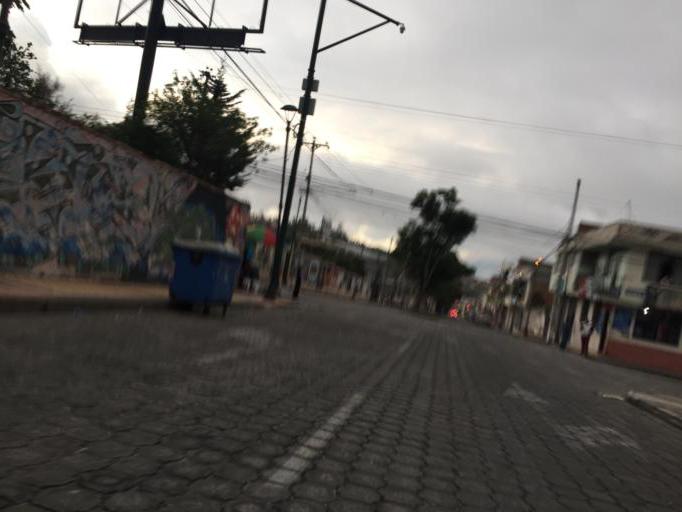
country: EC
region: Imbabura
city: Atuntaqui
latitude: 0.3355
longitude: -78.1704
